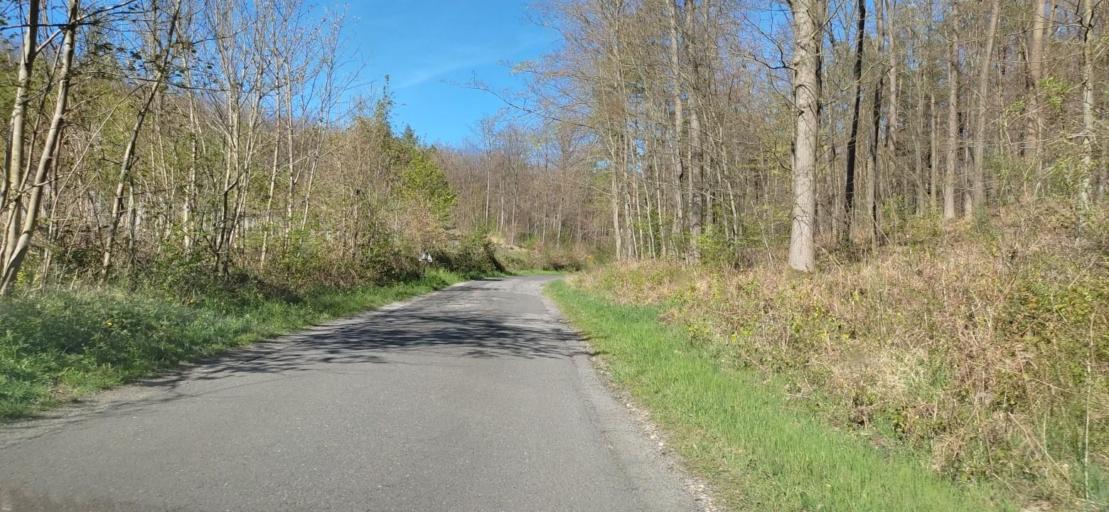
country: FR
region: Picardie
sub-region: Departement de l'Oise
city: Le Plessis-Brion
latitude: 49.4384
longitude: 2.9130
